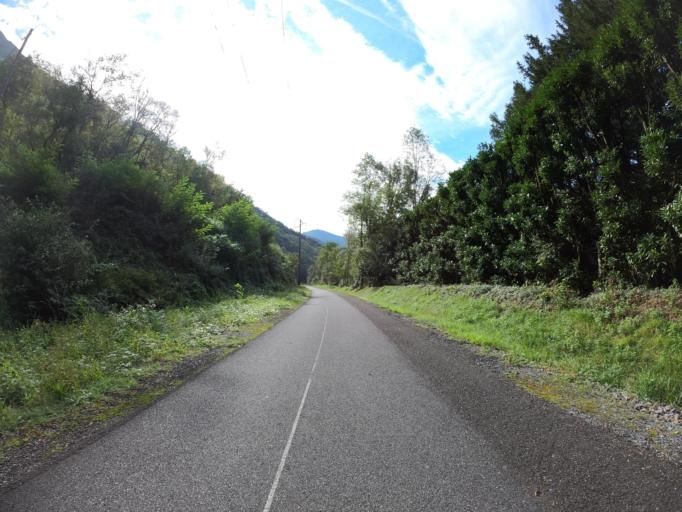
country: FR
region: Midi-Pyrenees
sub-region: Departement des Hautes-Pyrenees
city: Lourdes
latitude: 43.0760
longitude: -0.0411
